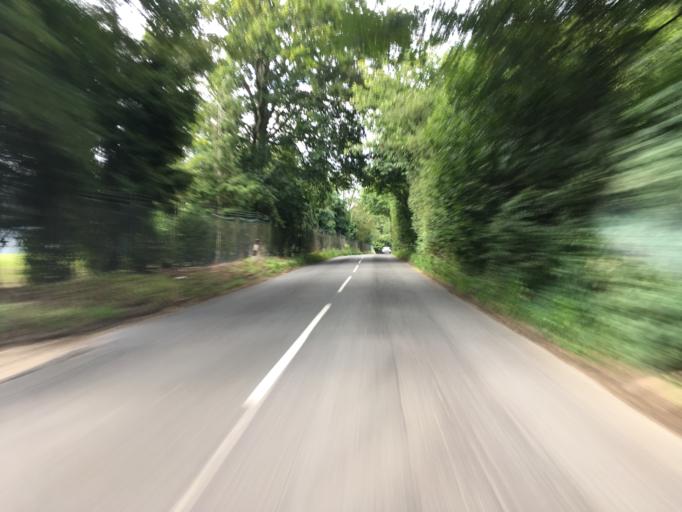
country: GB
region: England
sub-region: Hampshire
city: Overton
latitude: 51.1714
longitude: -1.2339
